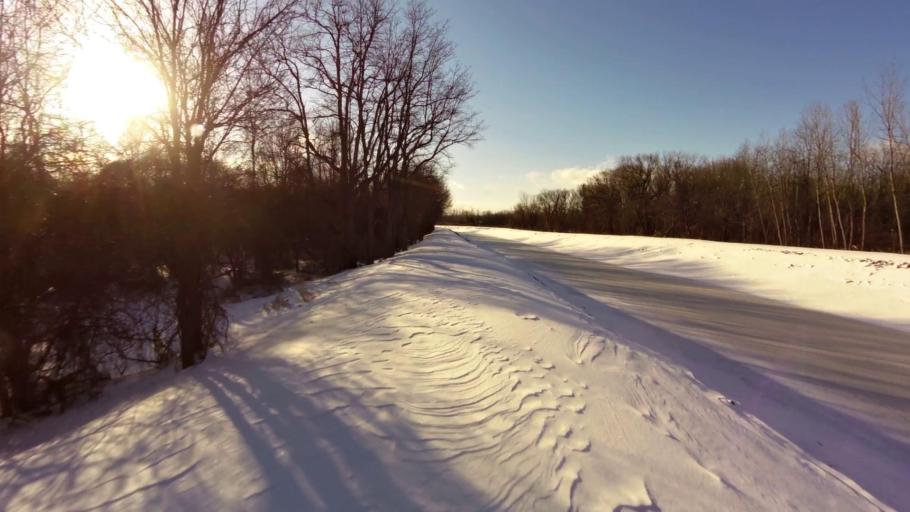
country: US
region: New York
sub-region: Orleans County
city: Albion
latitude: 43.2538
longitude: -78.2211
